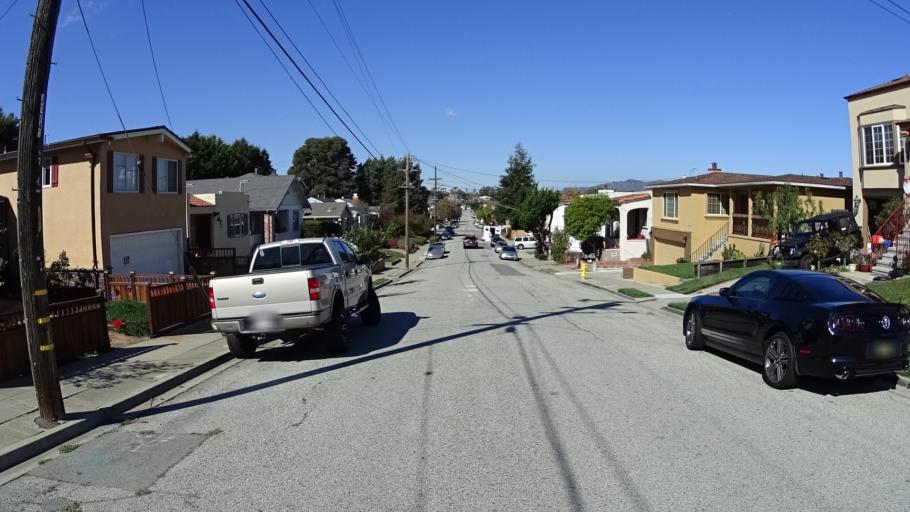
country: US
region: California
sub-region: San Mateo County
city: San Bruno
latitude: 37.6195
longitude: -122.4172
